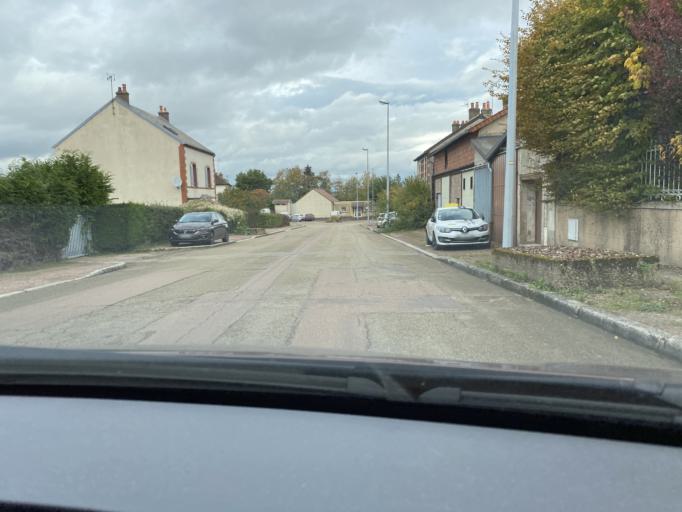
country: FR
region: Bourgogne
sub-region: Departement de la Cote-d'Or
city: Saulieu
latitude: 47.2820
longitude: 4.2348
